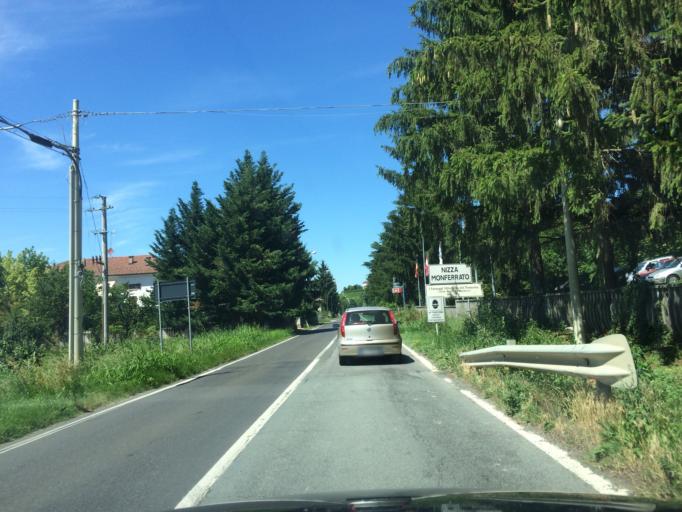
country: IT
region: Piedmont
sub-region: Provincia di Asti
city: Nizza Monferrato
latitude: 44.7612
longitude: 8.3694
